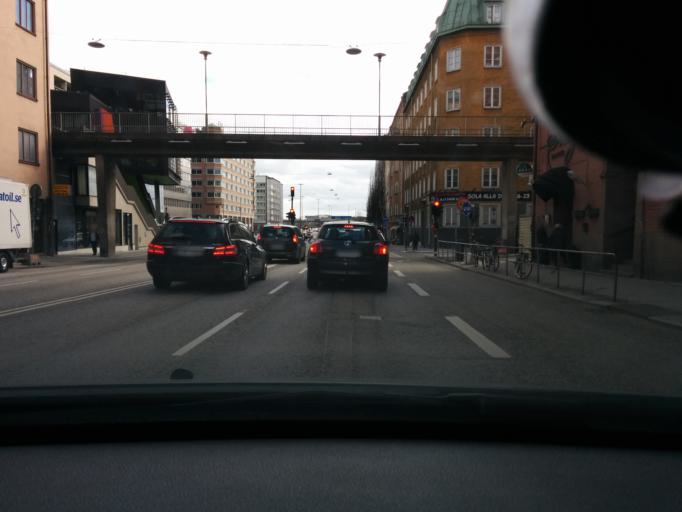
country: SE
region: Stockholm
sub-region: Stockholms Kommun
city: Arsta
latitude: 59.3172
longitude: 18.0329
